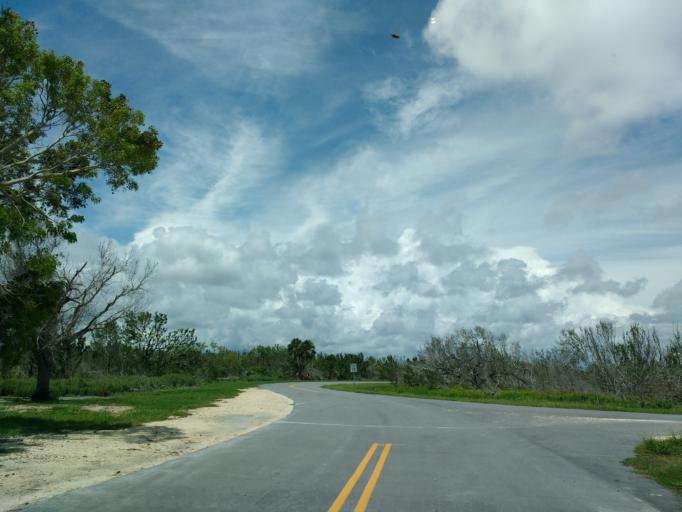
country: US
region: Florida
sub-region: Monroe County
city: Islamorada
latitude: 25.1376
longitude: -80.9385
